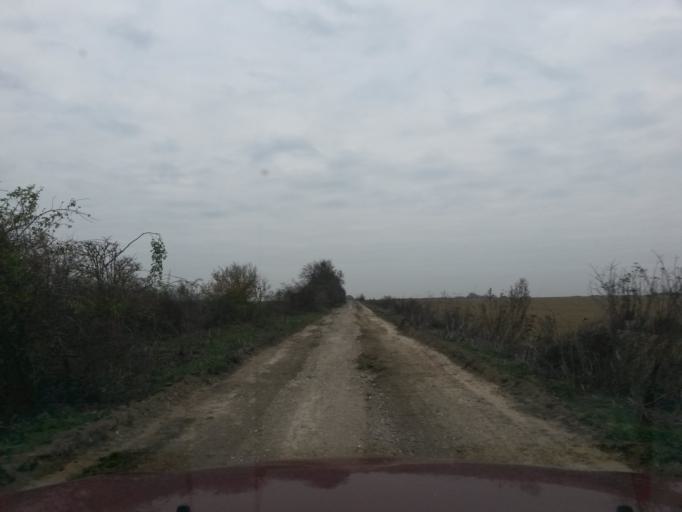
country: SK
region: Kosicky
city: Secovce
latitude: 48.6600
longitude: 21.6692
